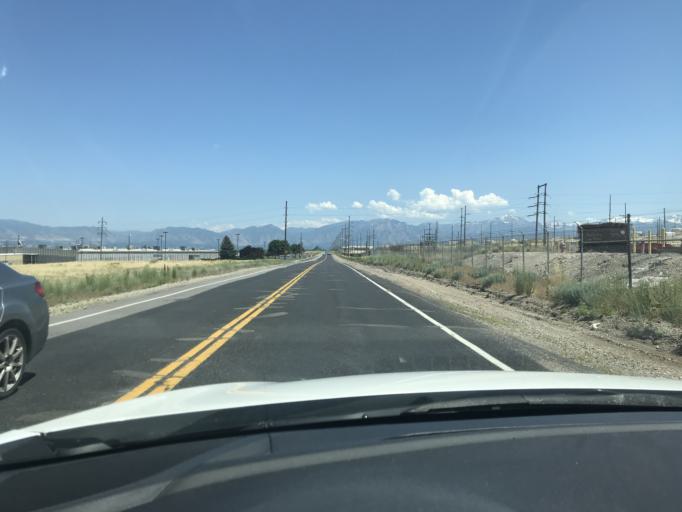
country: US
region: Utah
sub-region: Salt Lake County
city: Magna
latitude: 40.6820
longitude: -112.0802
